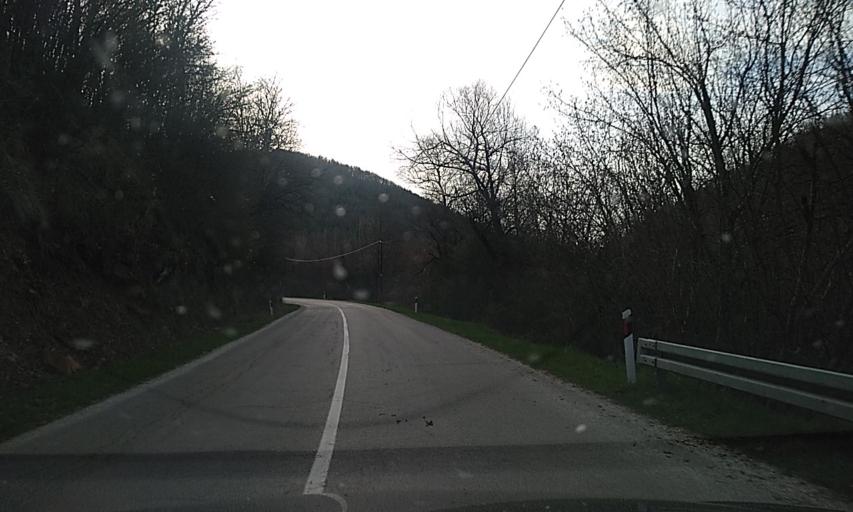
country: RS
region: Central Serbia
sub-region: Pcinjski Okrug
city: Bosilegrad
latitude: 42.4444
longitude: 22.5061
